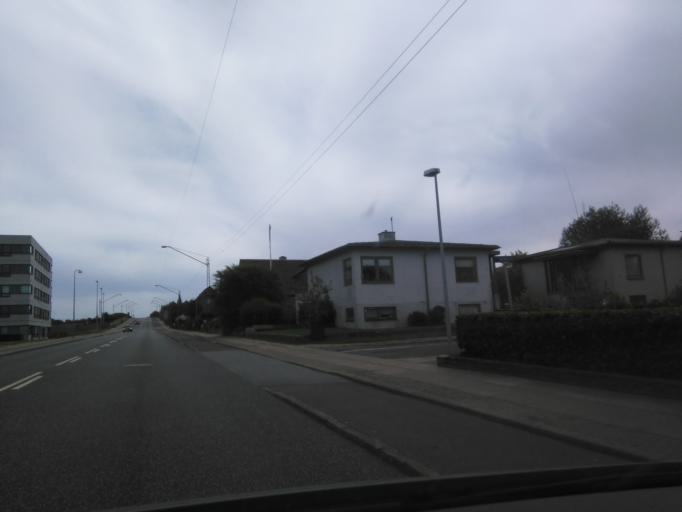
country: DK
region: Central Jutland
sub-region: Horsens Kommune
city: Horsens
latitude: 55.8708
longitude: 9.8566
